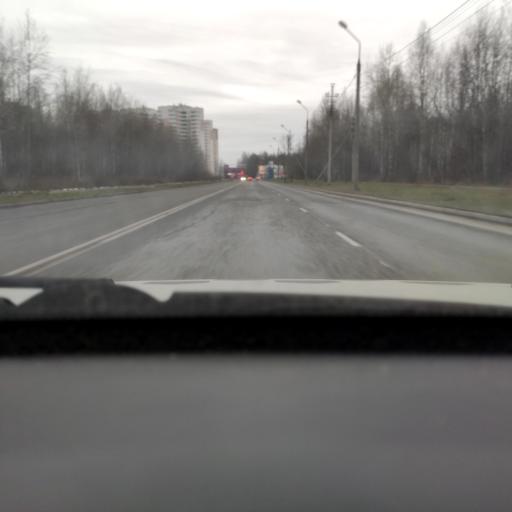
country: RU
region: Perm
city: Polazna
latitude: 58.1304
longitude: 56.4056
